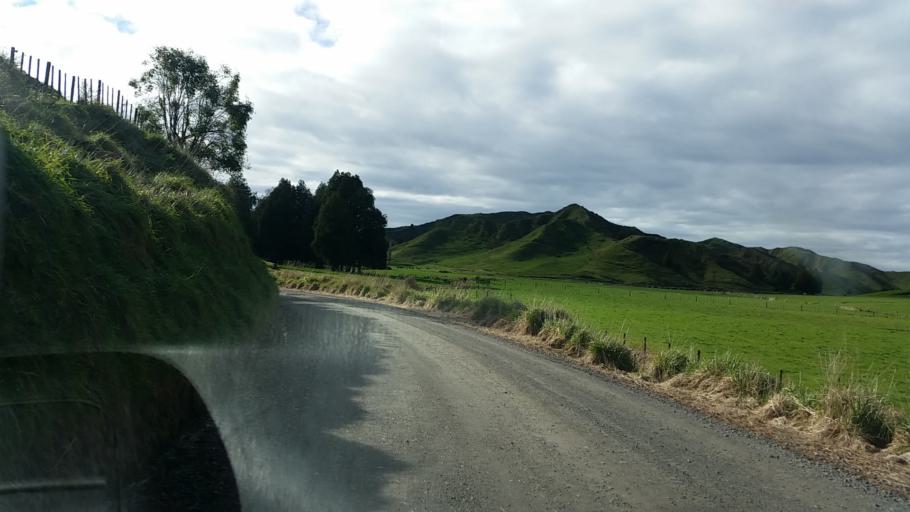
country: NZ
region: Taranaki
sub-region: South Taranaki District
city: Eltham
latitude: -39.2566
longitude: 174.5248
